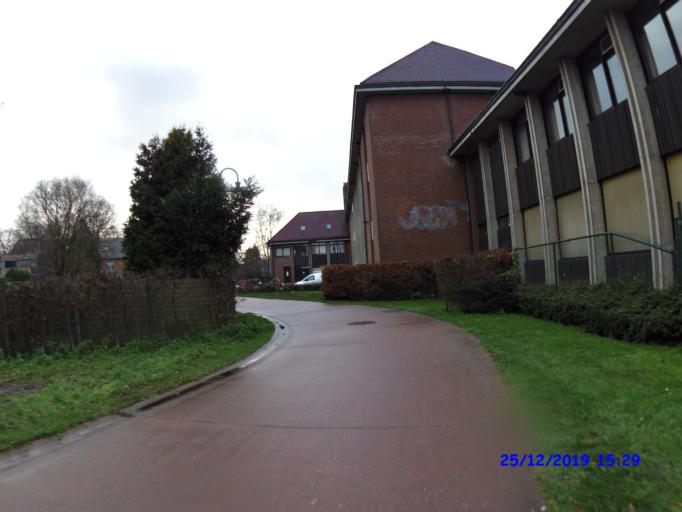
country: BE
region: Flanders
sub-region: Provincie Antwerpen
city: Geel
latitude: 51.1656
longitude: 4.9876
